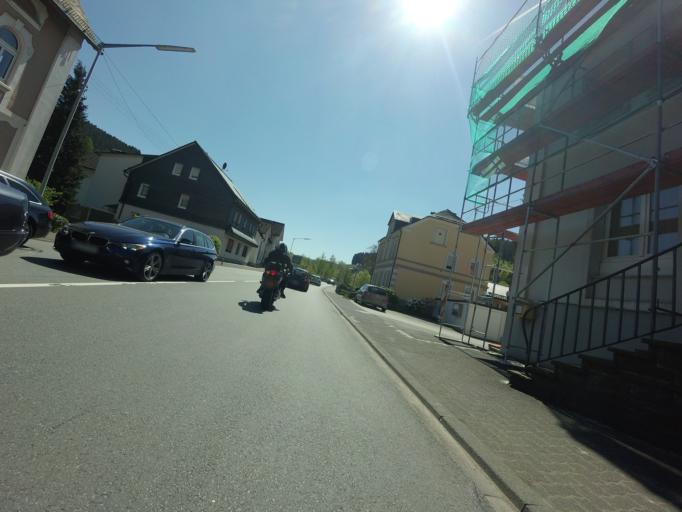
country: DE
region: North Rhine-Westphalia
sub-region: Regierungsbezirk Arnsberg
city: Kirchhundem
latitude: 51.0897
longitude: 8.0798
